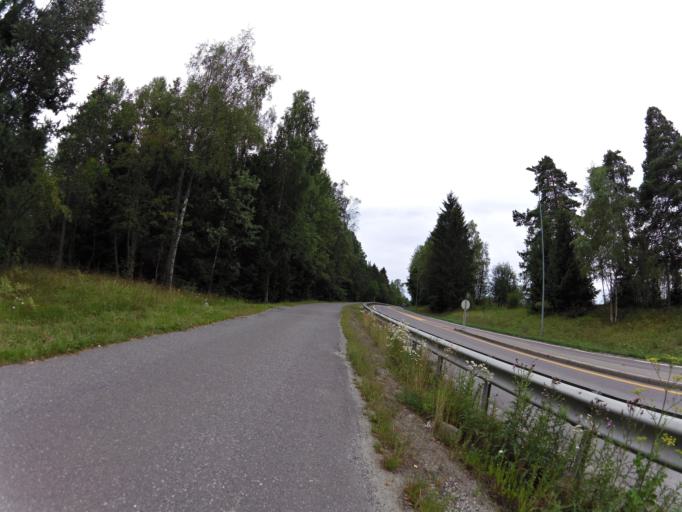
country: NO
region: Akershus
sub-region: Vestby
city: Vestby
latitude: 59.5864
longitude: 10.7465
